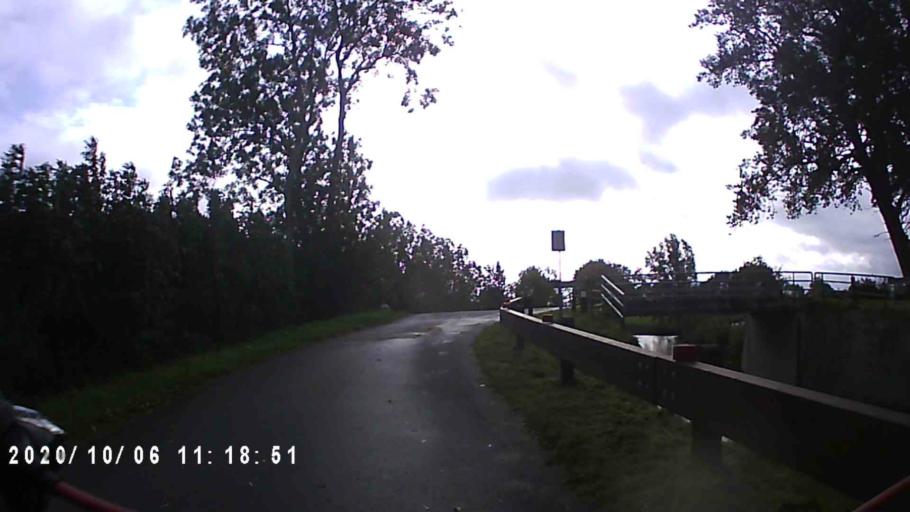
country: NL
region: Groningen
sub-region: Gemeente Zuidhorn
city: Oldehove
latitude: 53.3507
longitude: 6.3920
